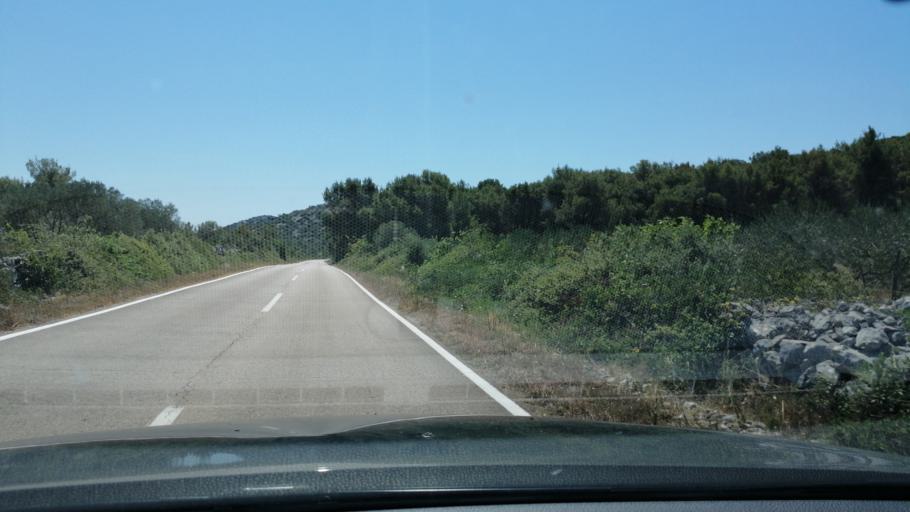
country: HR
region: Sibensko-Kniniska
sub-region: Grad Sibenik
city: Pirovac
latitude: 43.8421
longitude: 15.6883
